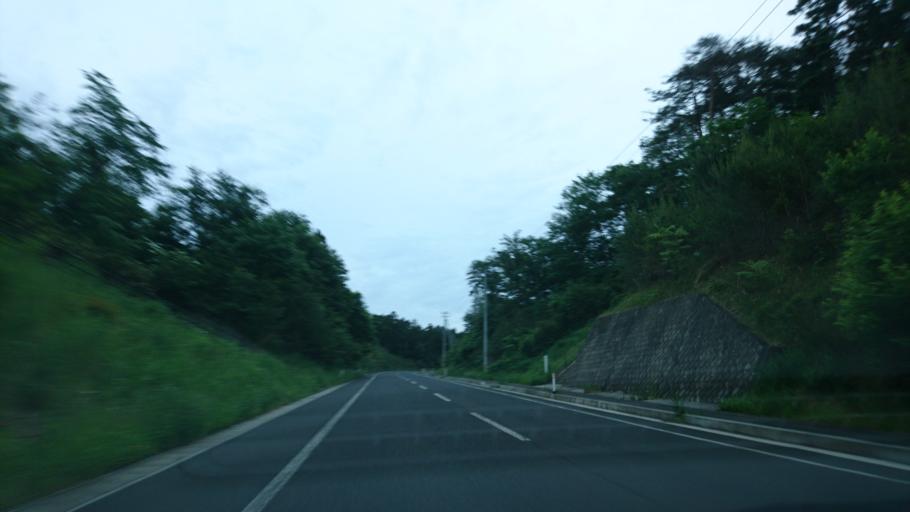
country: JP
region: Iwate
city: Ichinoseki
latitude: 38.9139
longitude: 141.1740
